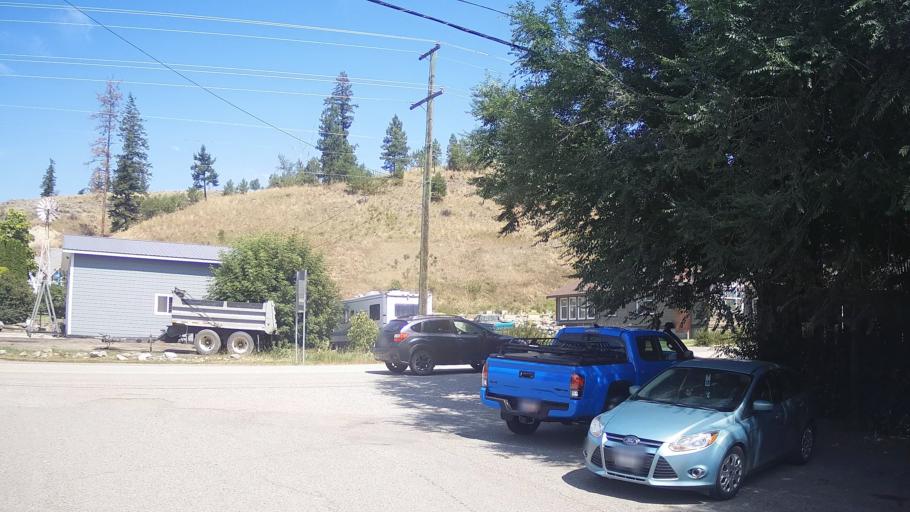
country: CA
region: British Columbia
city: Kamloops
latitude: 50.8602
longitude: -120.2645
